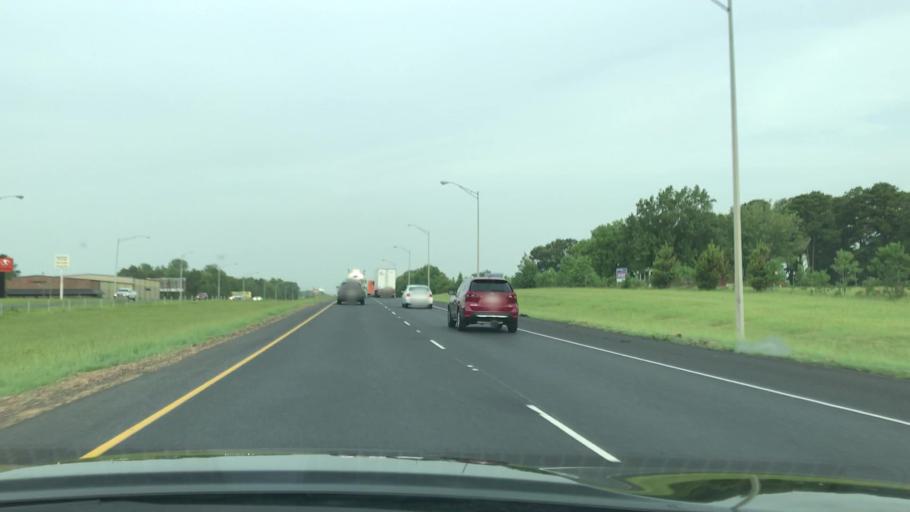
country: US
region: Louisiana
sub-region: Caddo Parish
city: Greenwood
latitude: 32.4479
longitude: -93.8880
